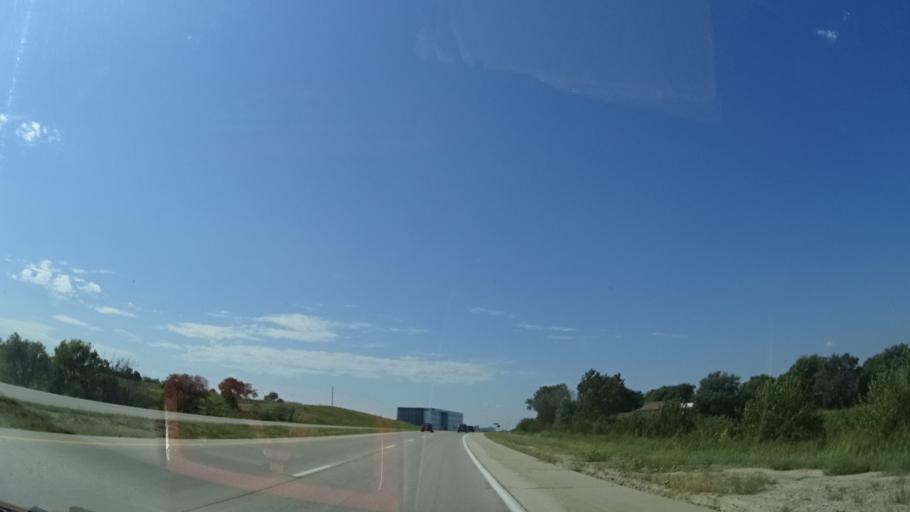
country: US
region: Nebraska
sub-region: Sarpy County
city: Papillion
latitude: 41.1370
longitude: -96.0171
